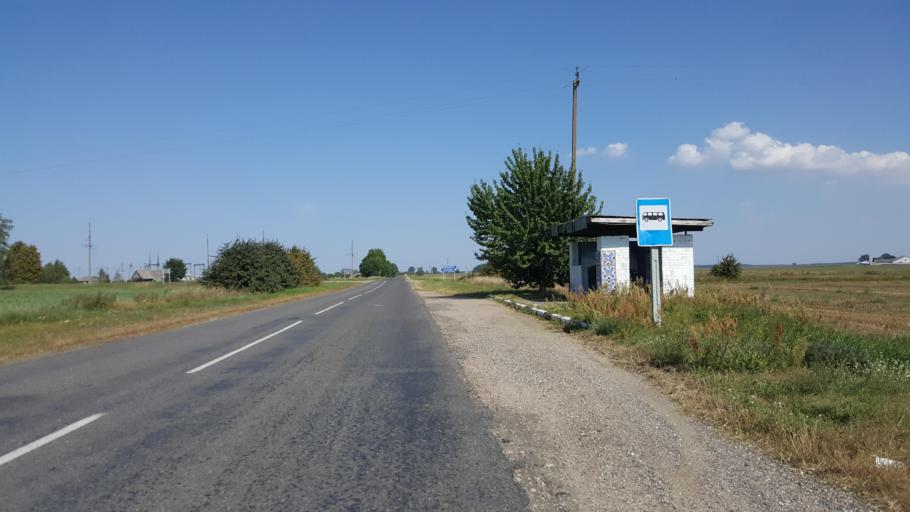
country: PL
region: Podlasie
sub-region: Powiat hajnowski
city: Czeremcha
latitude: 52.4820
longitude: 23.5364
